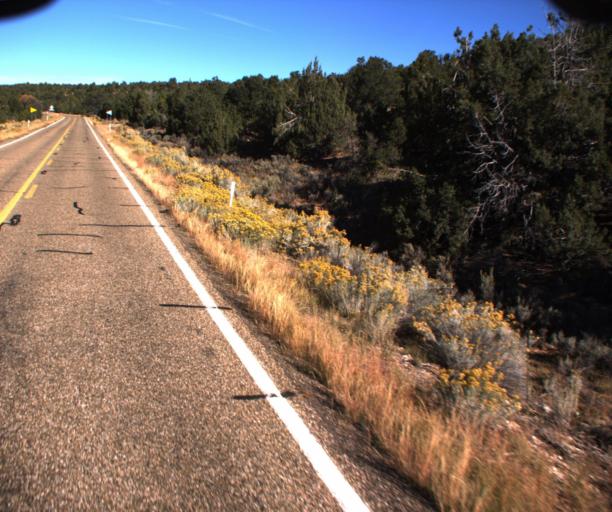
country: US
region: Arizona
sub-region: Coconino County
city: Fredonia
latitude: 36.7341
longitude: -112.0975
